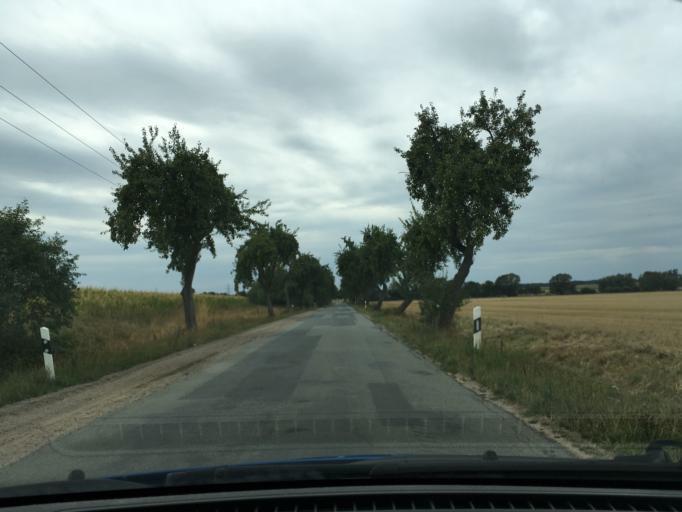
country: DE
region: Mecklenburg-Vorpommern
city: Wittenburg
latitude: 53.5158
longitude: 11.1332
